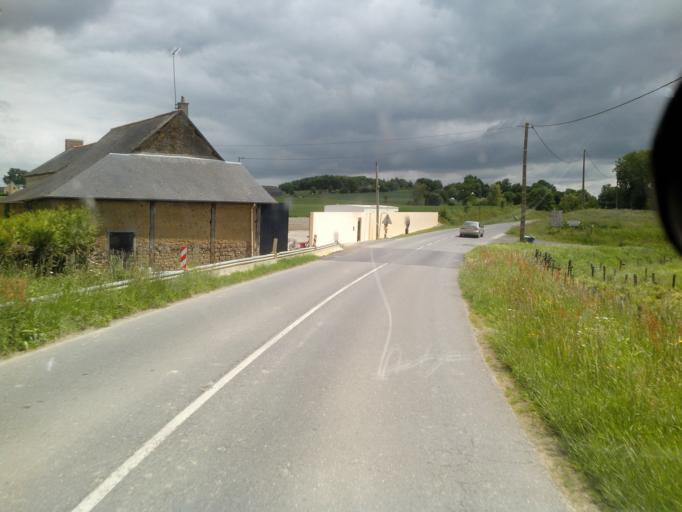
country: FR
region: Brittany
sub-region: Departement d'Ille-et-Vilaine
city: Chasne-sur-Illet
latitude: 48.2543
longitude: -1.5837
